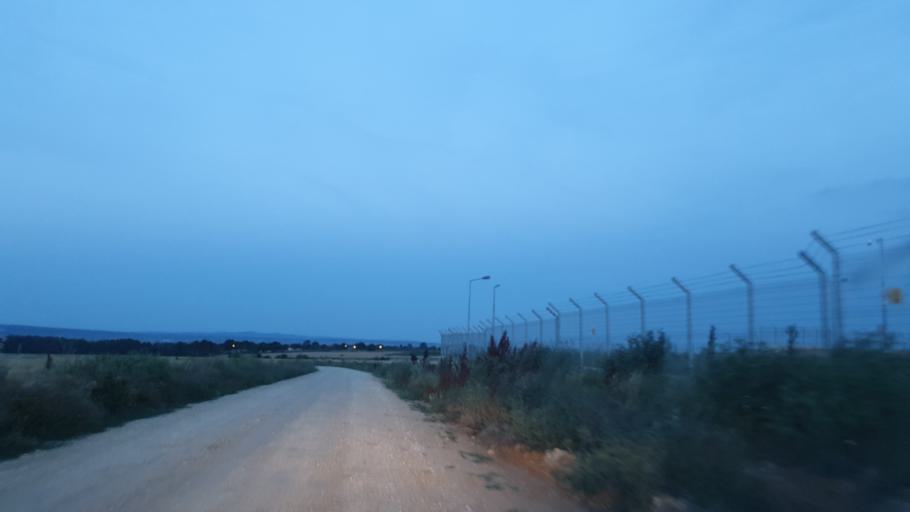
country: TR
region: Kirklareli
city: Vize
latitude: 41.5179
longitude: 27.7623
